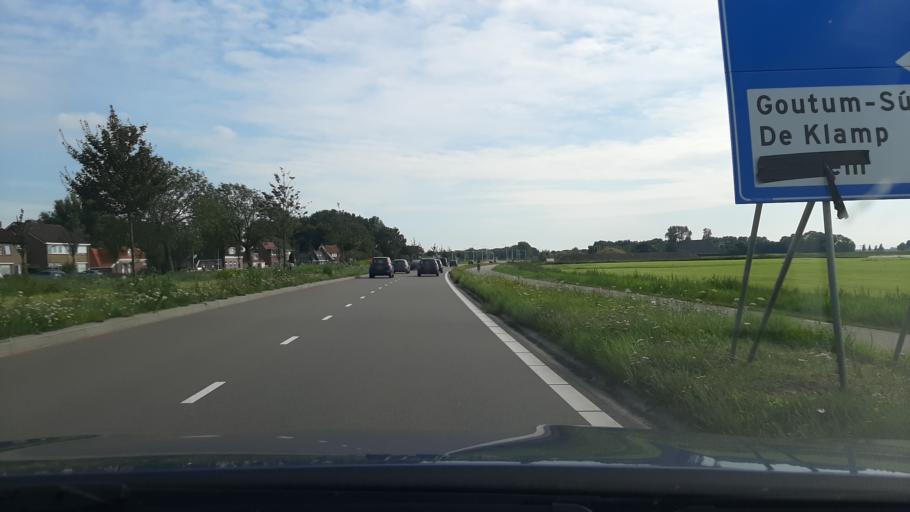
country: NL
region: Friesland
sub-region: Gemeente Leeuwarden
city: Goutum
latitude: 53.1766
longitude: 5.7948
